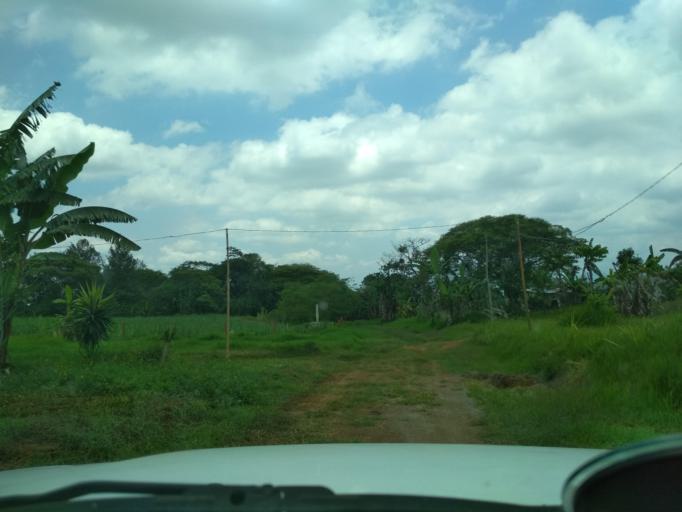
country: MX
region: Veracruz
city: Tocuila
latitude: 18.9466
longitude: -97.0153
